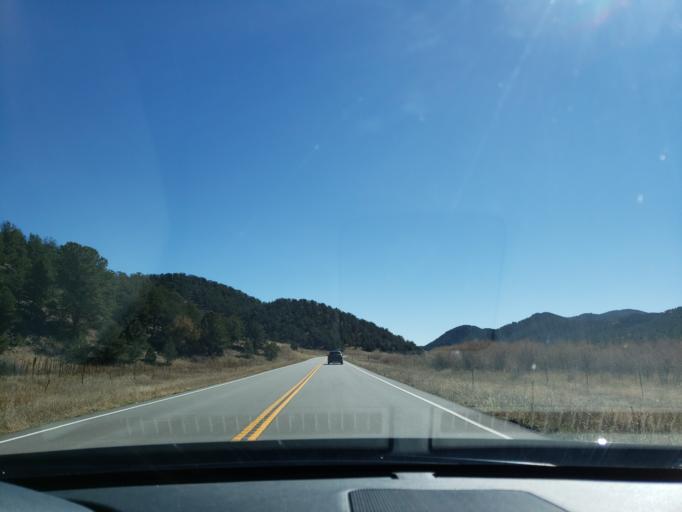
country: US
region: Colorado
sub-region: Fremont County
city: Canon City
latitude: 38.6351
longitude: -105.4647
